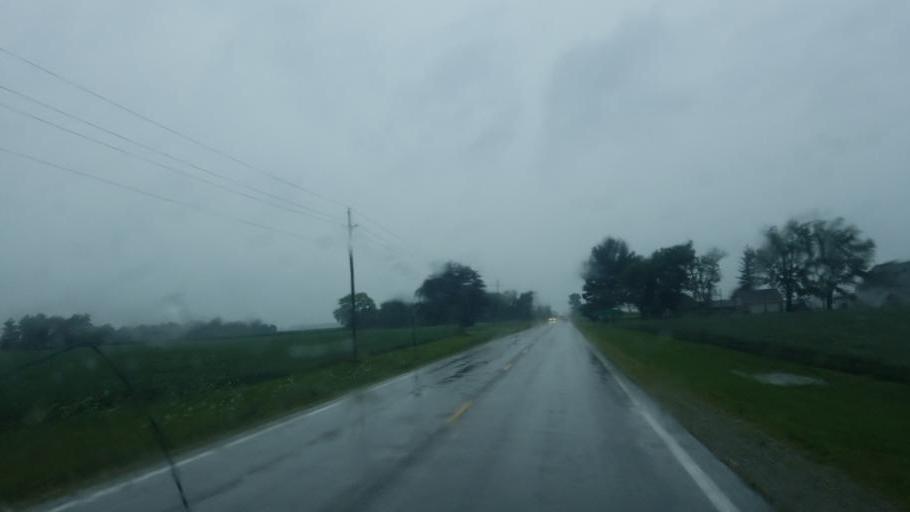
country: US
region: Indiana
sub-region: Blackford County
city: Montpelier
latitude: 40.6545
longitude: -85.2745
